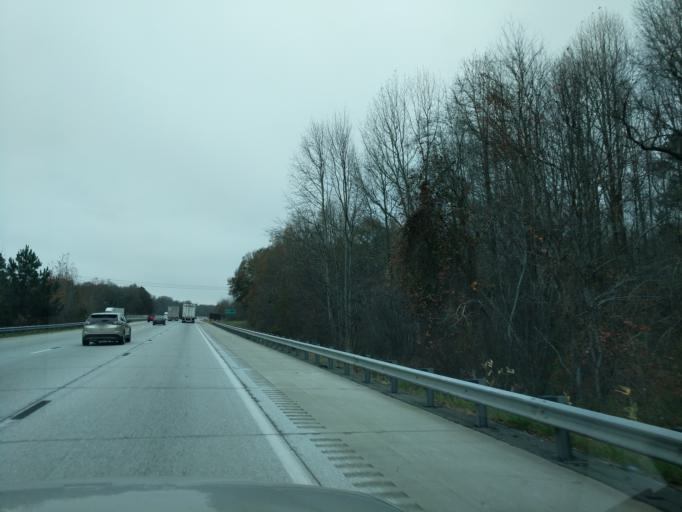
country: US
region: South Carolina
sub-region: Anderson County
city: Piedmont
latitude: 34.6926
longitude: -82.5065
